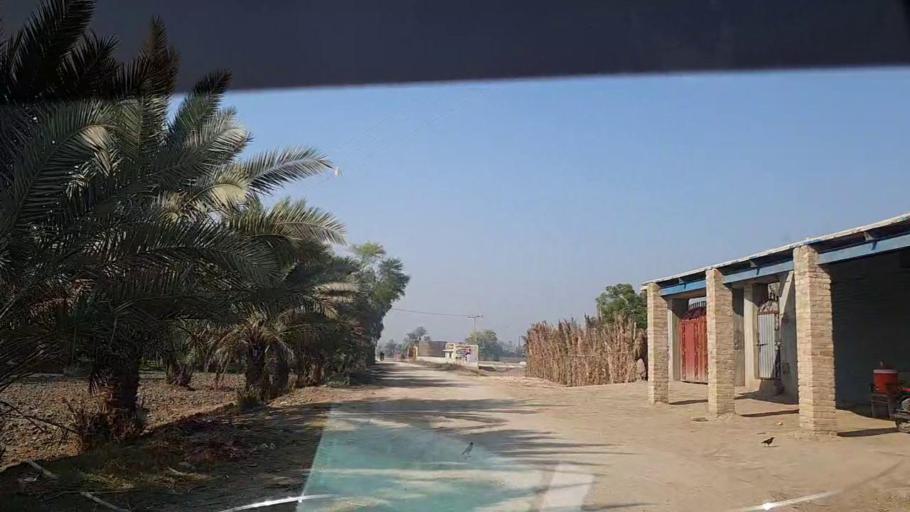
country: PK
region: Sindh
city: Khairpur
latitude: 27.4920
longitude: 68.7536
